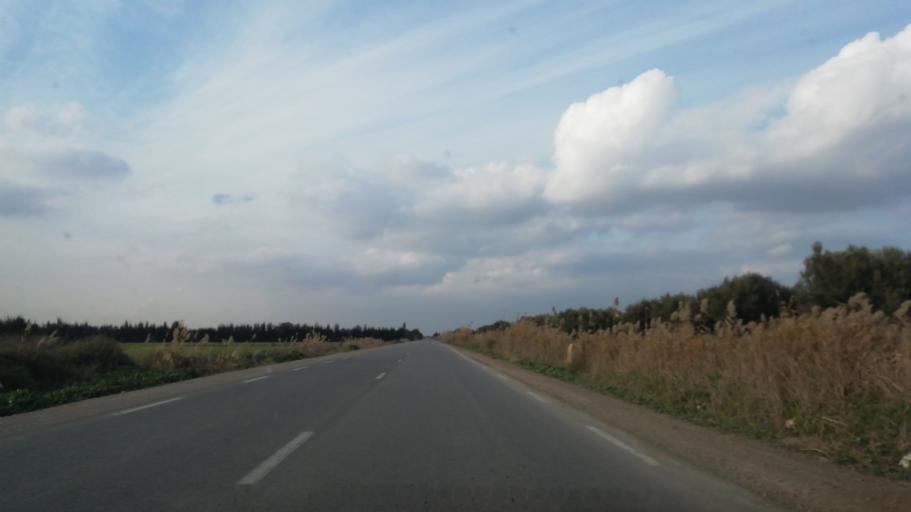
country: DZ
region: Mascara
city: Sig
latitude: 35.6403
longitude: 0.0321
